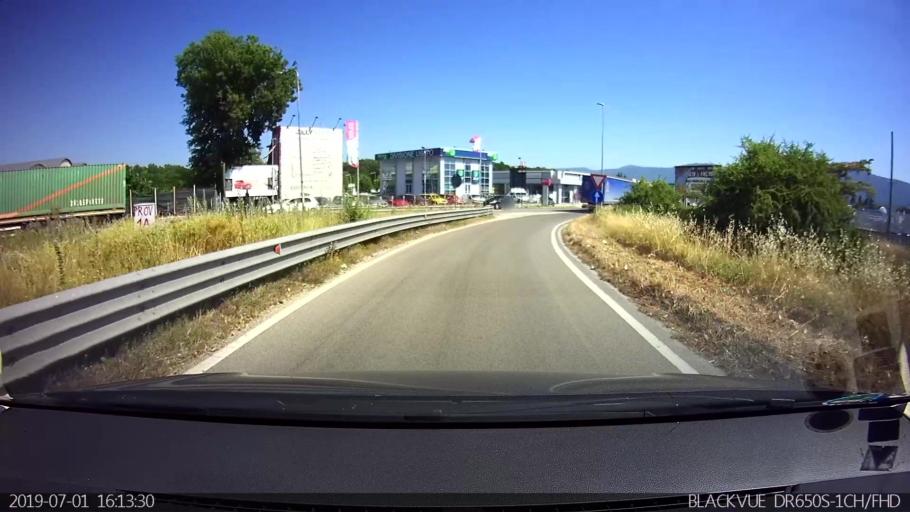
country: IT
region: Latium
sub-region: Provincia di Frosinone
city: Ceccano
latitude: 41.6072
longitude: 13.3002
